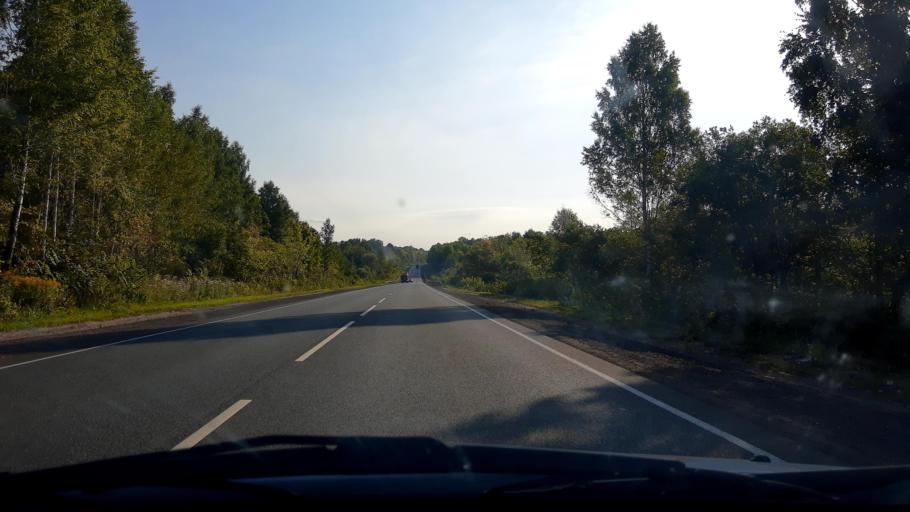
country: RU
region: Bashkortostan
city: Oktyabr'skiy
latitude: 54.4453
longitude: 53.5670
